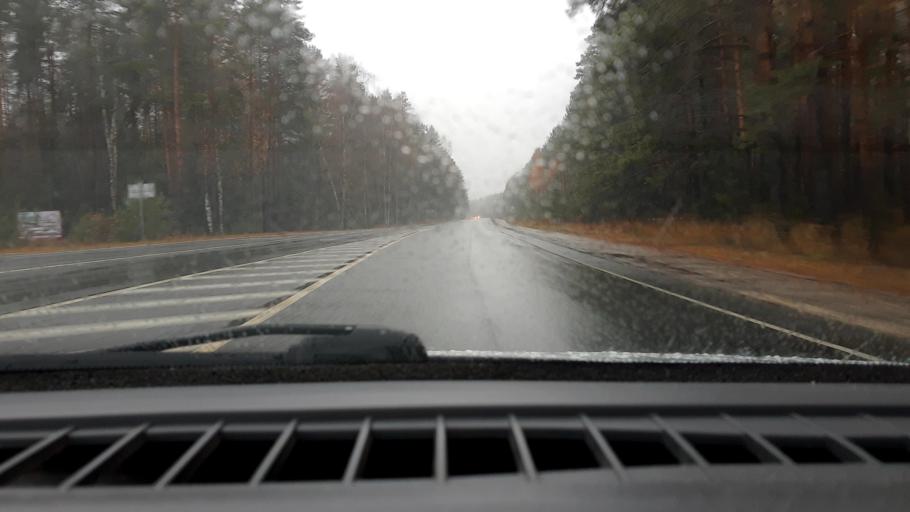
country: RU
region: Nizjnij Novgorod
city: Linda
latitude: 56.6853
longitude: 44.1766
